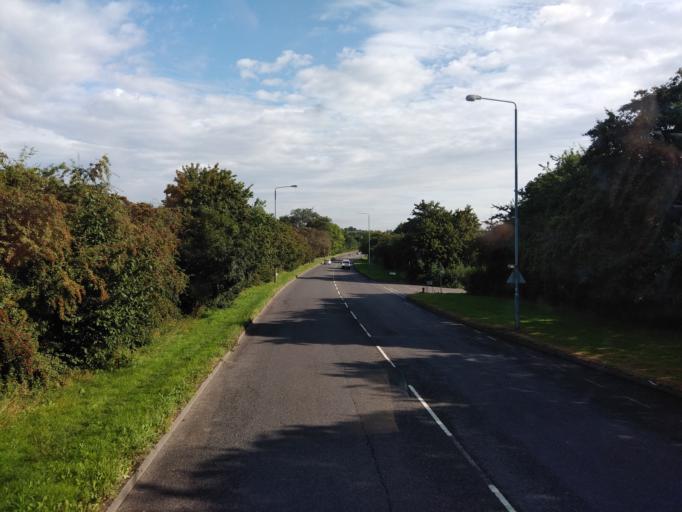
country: GB
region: England
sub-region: Nottinghamshire
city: Kimberley
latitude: 52.9572
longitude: -1.2450
